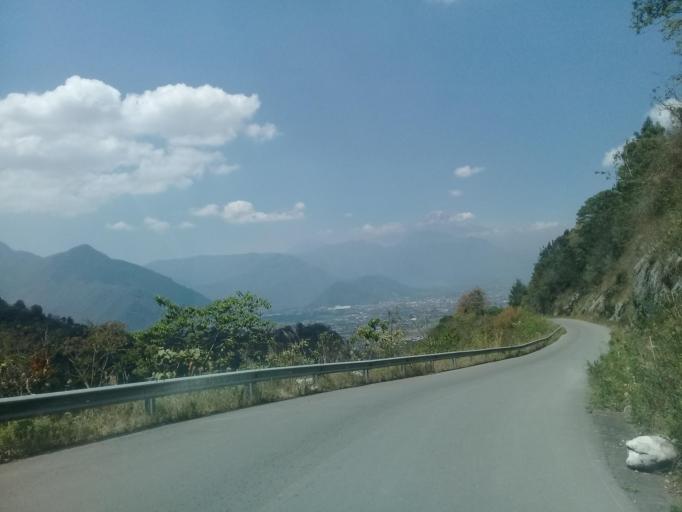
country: MX
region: Veracruz
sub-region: Tlilapan
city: Tonalixco
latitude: 18.7989
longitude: -97.0569
